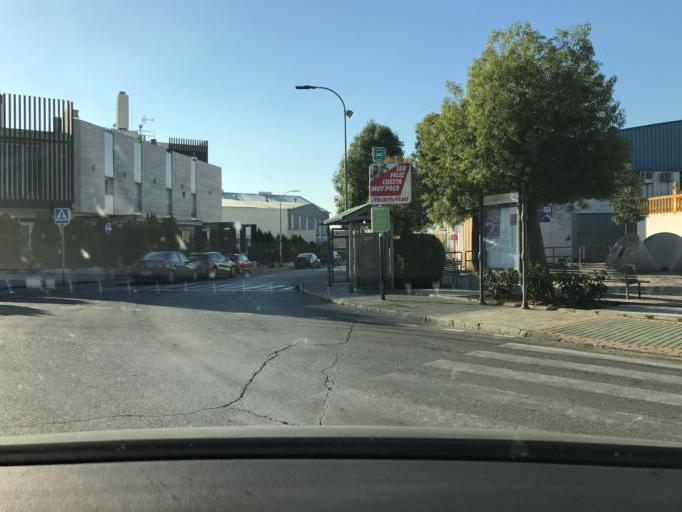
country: ES
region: Andalusia
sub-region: Provincia de Granada
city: Peligros
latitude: 37.2278
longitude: -3.6293
